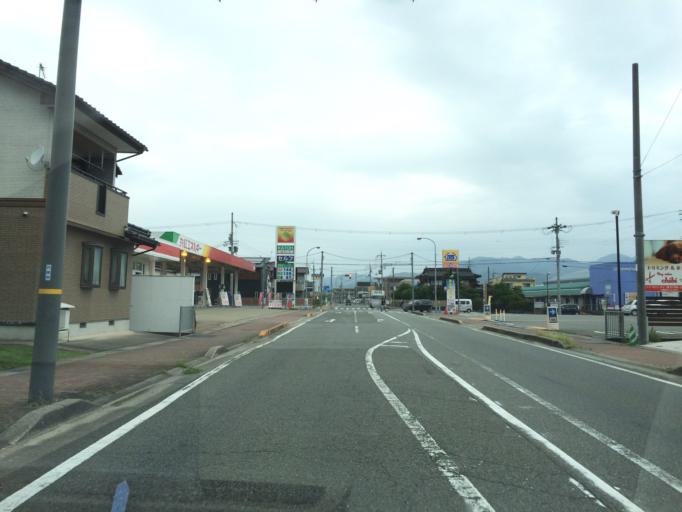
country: JP
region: Hyogo
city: Toyooka
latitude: 35.5407
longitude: 134.8095
